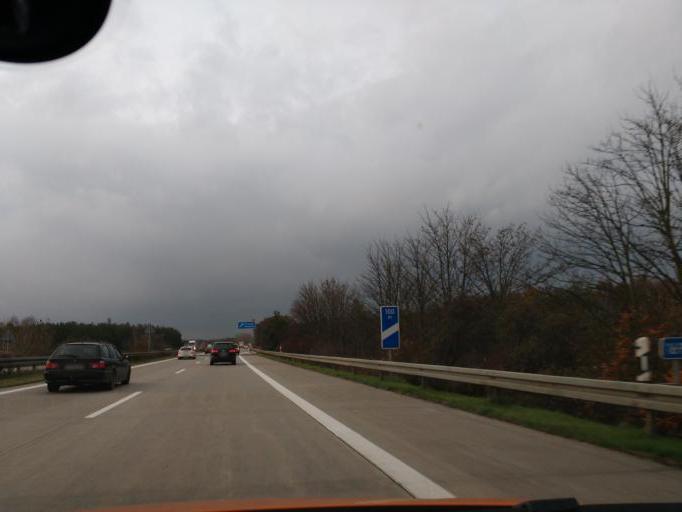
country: DE
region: Brandenburg
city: Heiligengrabe
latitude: 53.1479
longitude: 12.4088
